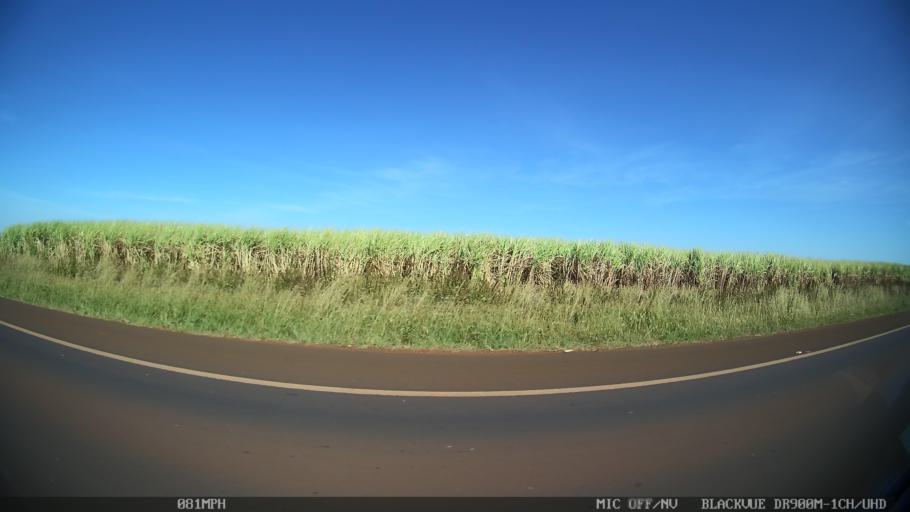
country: BR
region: Sao Paulo
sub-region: Guaira
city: Guaira
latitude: -20.4439
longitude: -48.3482
